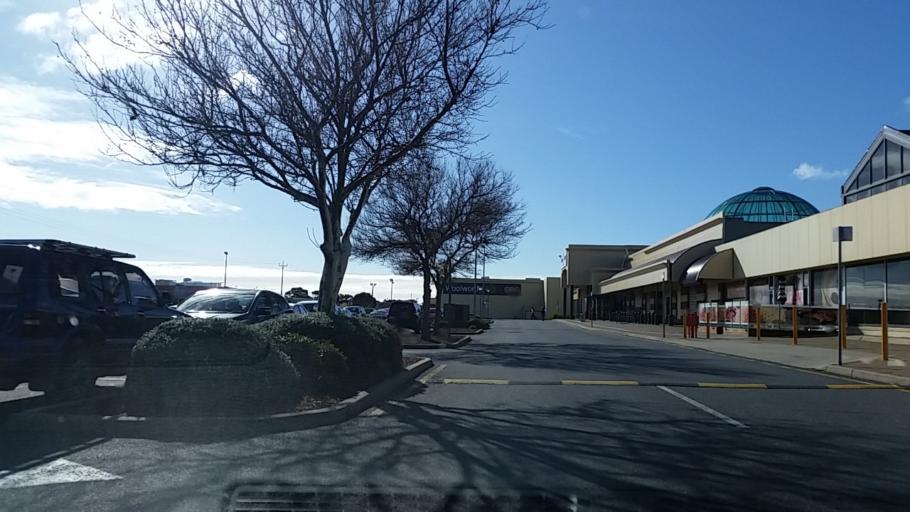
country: AU
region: South Australia
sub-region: Onkaparinga
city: Seaford
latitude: -35.1903
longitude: 138.4788
